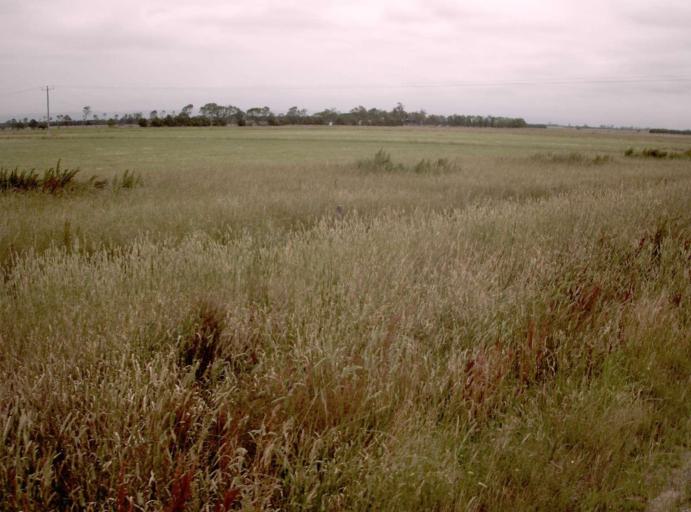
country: AU
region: Victoria
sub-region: Wellington
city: Heyfield
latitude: -38.0998
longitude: 146.7733
